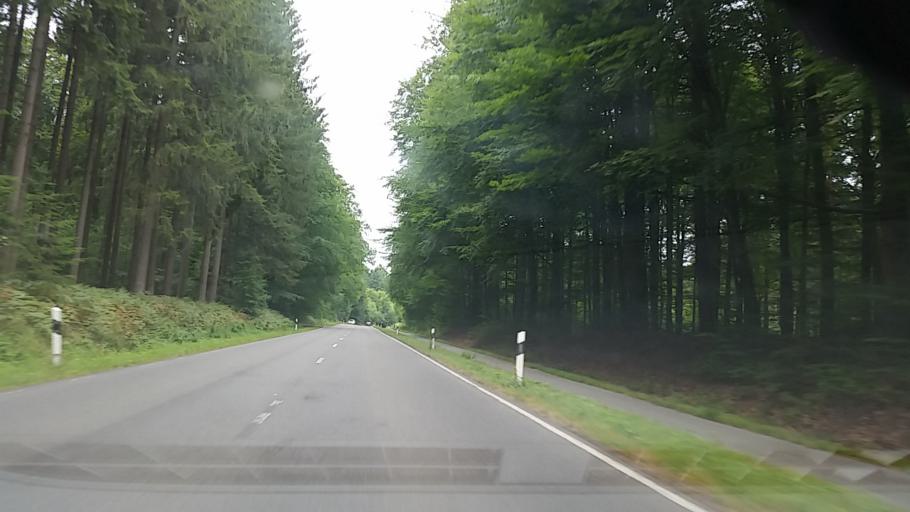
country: DE
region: Schleswig-Holstein
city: Aumuhle
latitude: 53.5184
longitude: 10.3481
